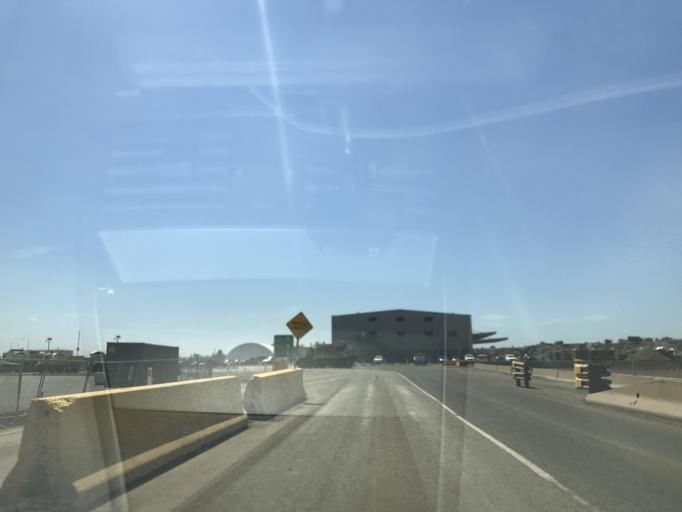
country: AU
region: Victoria
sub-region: Wyndham
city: Truganina
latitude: -37.8319
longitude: 144.7718
